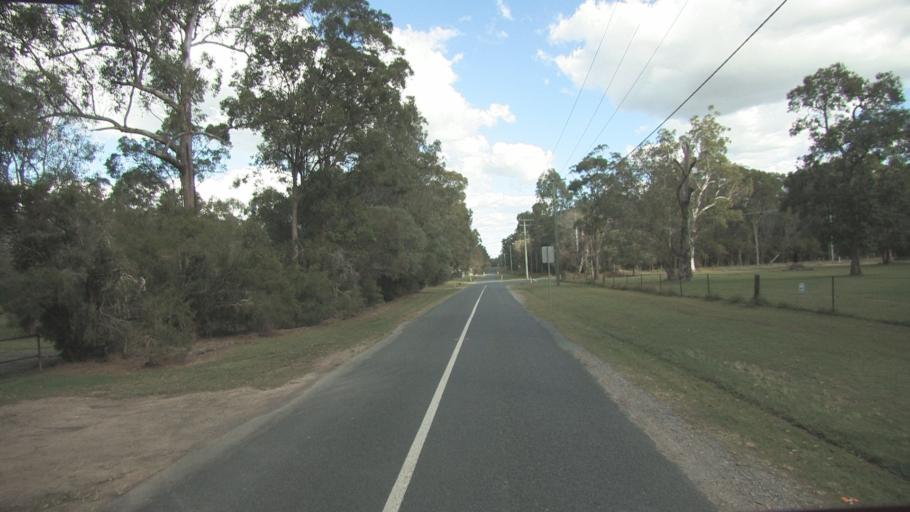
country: AU
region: Queensland
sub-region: Gold Coast
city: Yatala
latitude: -27.6605
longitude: 153.2415
